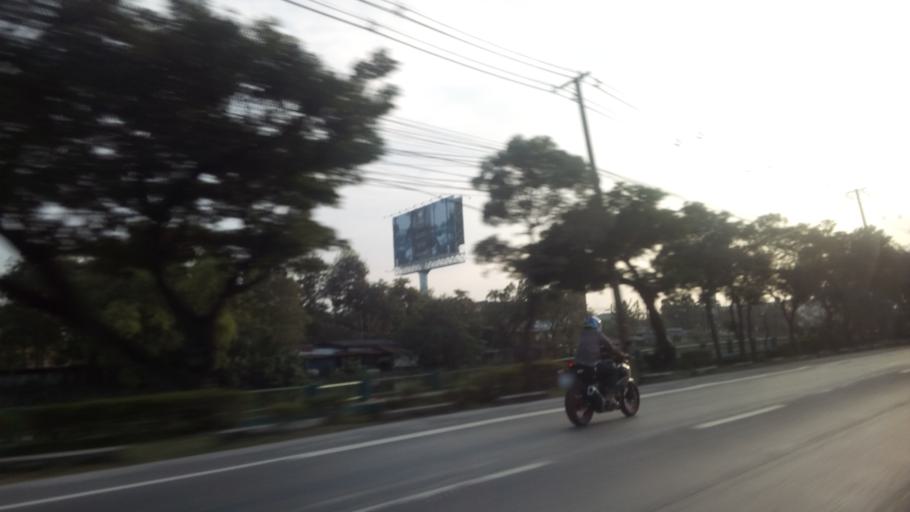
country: TH
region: Pathum Thani
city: Thanyaburi
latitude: 14.0042
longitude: 100.6971
